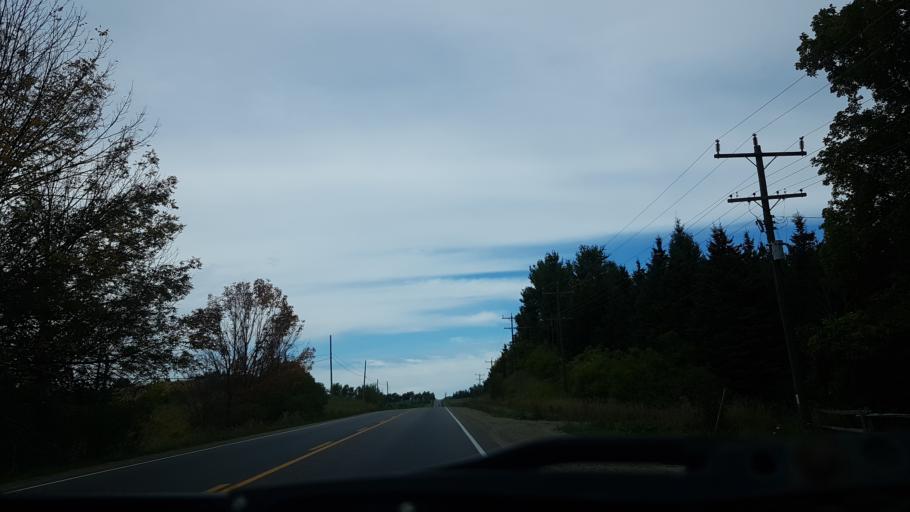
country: CA
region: Ontario
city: Wasaga Beach
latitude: 44.3475
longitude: -80.0806
